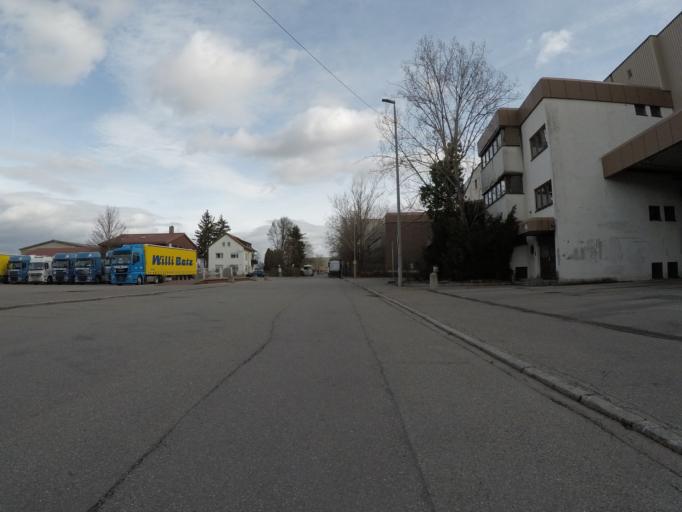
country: DE
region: Baden-Wuerttemberg
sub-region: Tuebingen Region
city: Reutlingen
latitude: 48.5083
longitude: 9.2187
